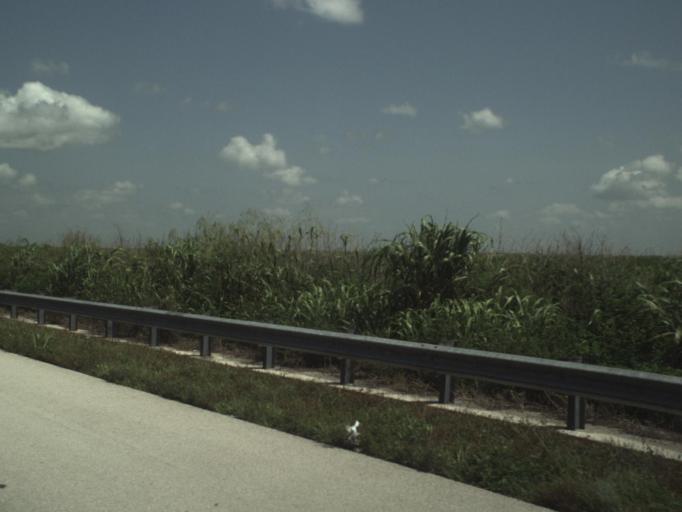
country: US
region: Florida
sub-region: Palm Beach County
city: Belle Glade Camp
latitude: 26.3809
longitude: -80.5732
